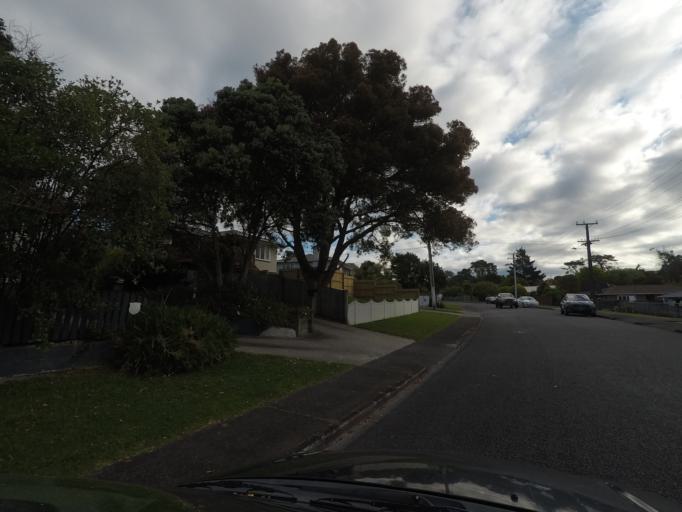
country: NZ
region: Auckland
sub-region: Auckland
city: Rosebank
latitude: -36.8828
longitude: 174.6559
